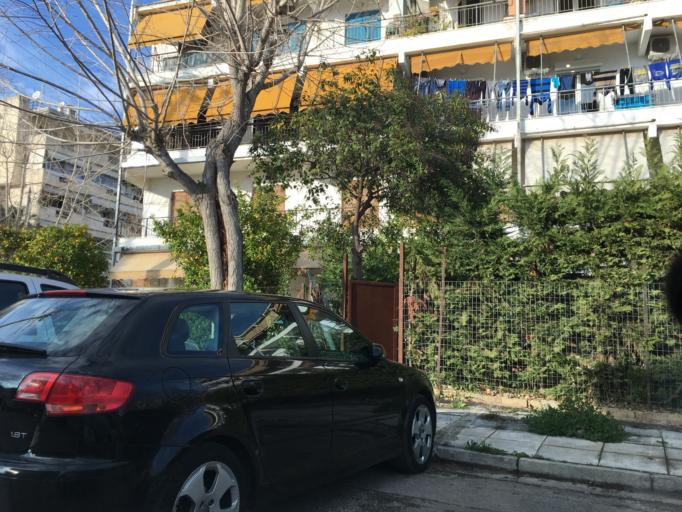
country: GR
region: Attica
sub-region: Nomarchia Athinas
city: Marousi
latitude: 38.0461
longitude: 23.8000
